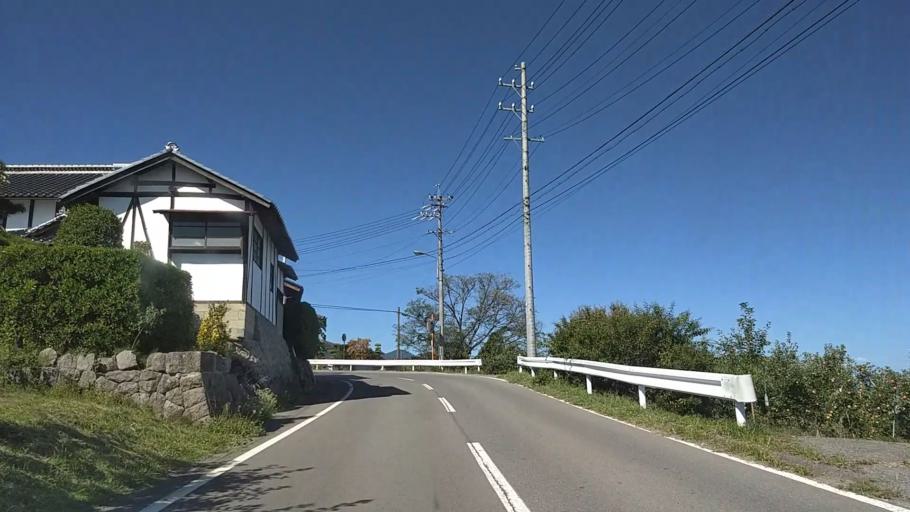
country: JP
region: Nagano
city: Nagano-shi
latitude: 36.5798
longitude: 138.1262
